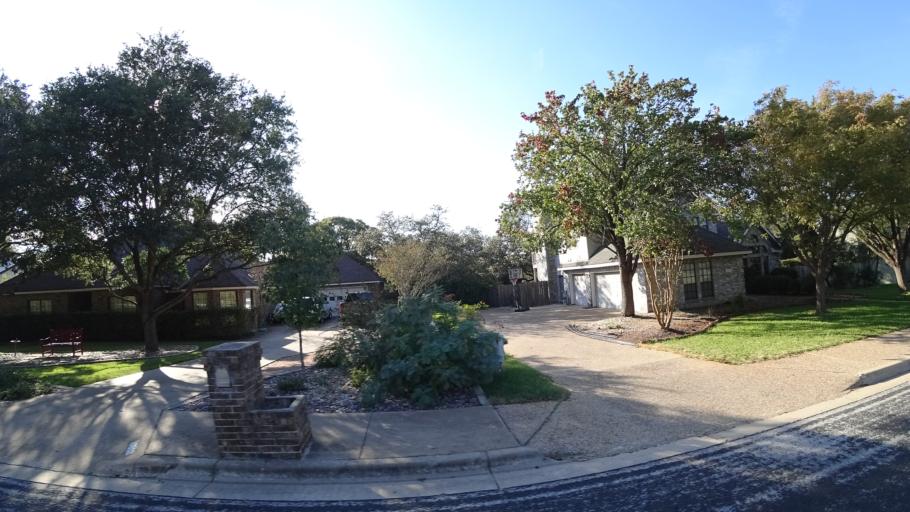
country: US
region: Texas
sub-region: Williamson County
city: Anderson Mill
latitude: 30.4375
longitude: -97.8109
